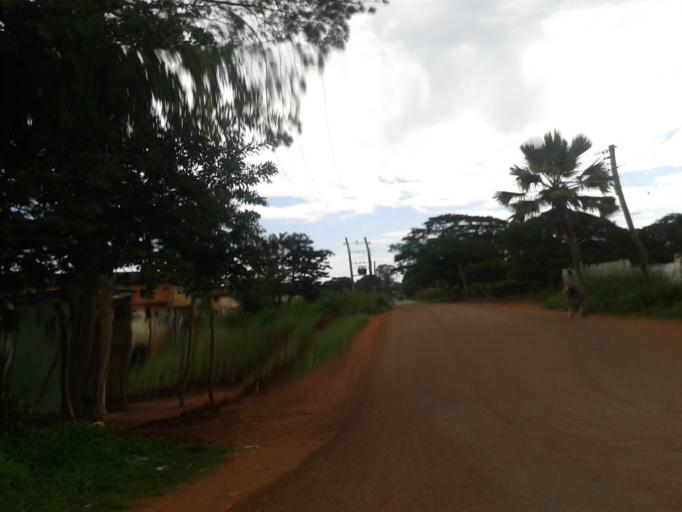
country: UG
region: Northern Region
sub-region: Gulu District
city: Gulu
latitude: 2.7847
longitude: 32.3075
